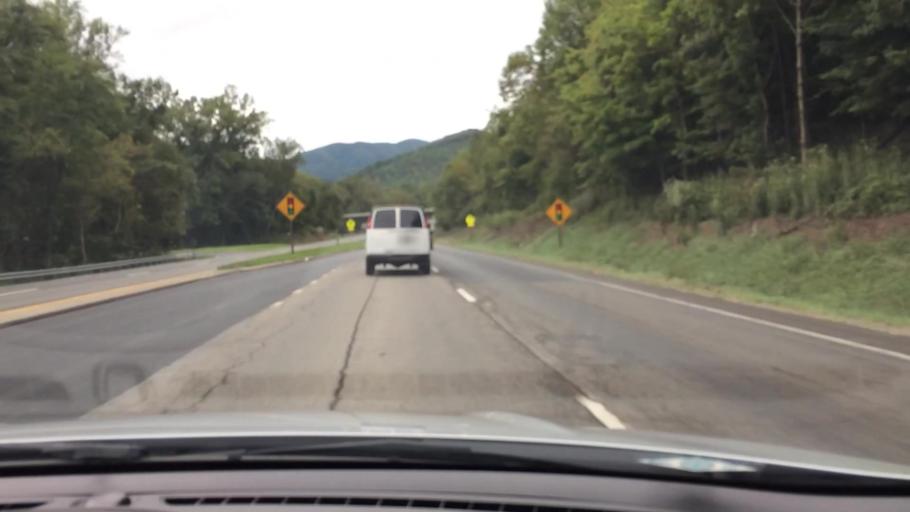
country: US
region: Virginia
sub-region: Roanoke County
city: Narrows
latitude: 37.2141
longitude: -79.9592
